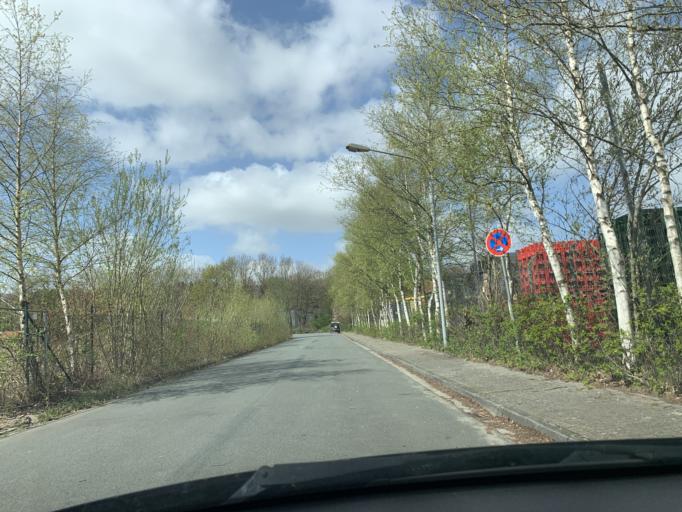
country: DE
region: Lower Saxony
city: Westerstede
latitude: 53.2682
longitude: 7.9422
